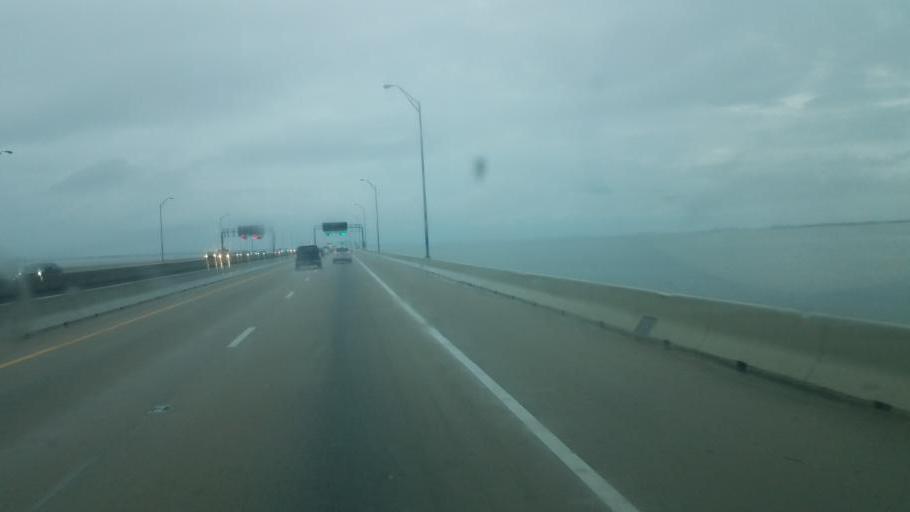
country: US
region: Virginia
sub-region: City of Newport News
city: Newport News
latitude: 36.9059
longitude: -76.4208
